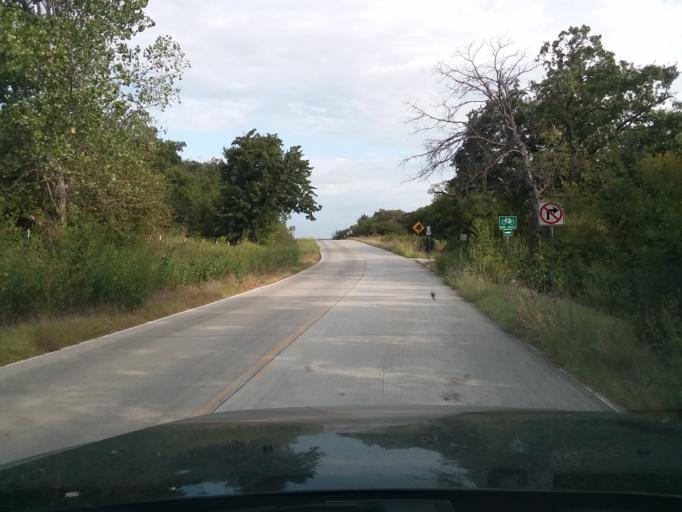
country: US
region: Texas
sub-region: Denton County
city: Copper Canyon
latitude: 33.1189
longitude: -97.1083
